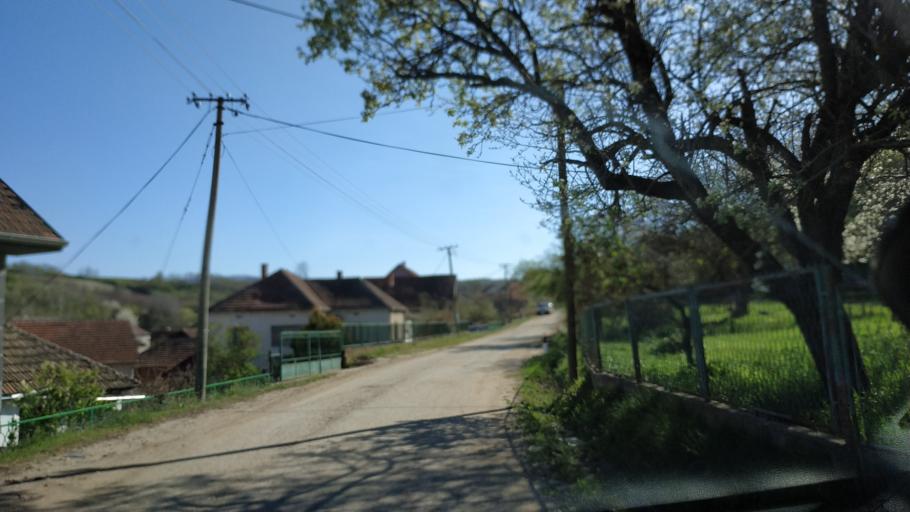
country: RS
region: Central Serbia
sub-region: Nisavski Okrug
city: Aleksinac
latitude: 43.4741
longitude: 21.6454
